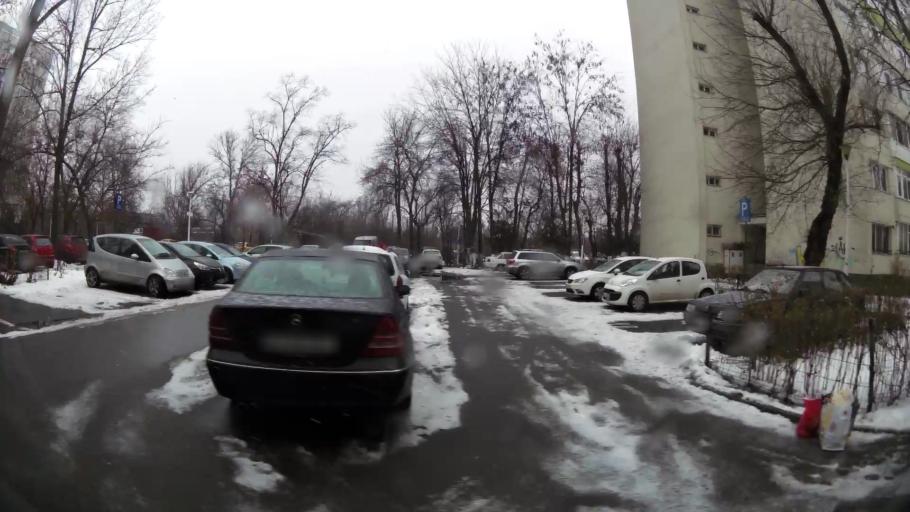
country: RO
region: Ilfov
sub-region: Comuna Chiajna
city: Rosu
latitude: 44.4796
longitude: 26.0516
